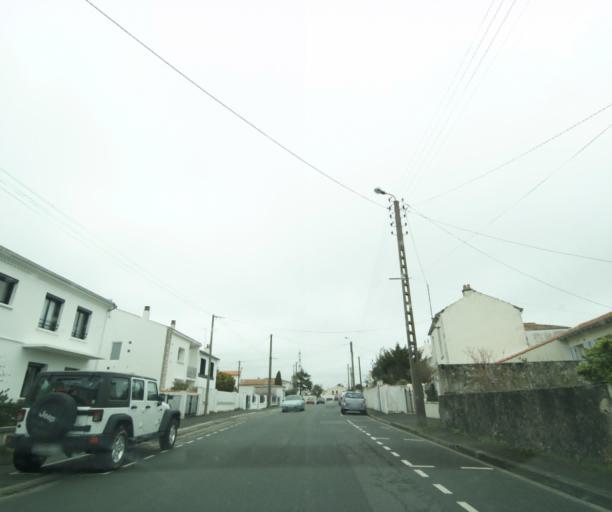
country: FR
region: Poitou-Charentes
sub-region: Departement de la Charente-Maritime
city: La Rochelle
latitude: 46.1788
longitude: -1.1407
